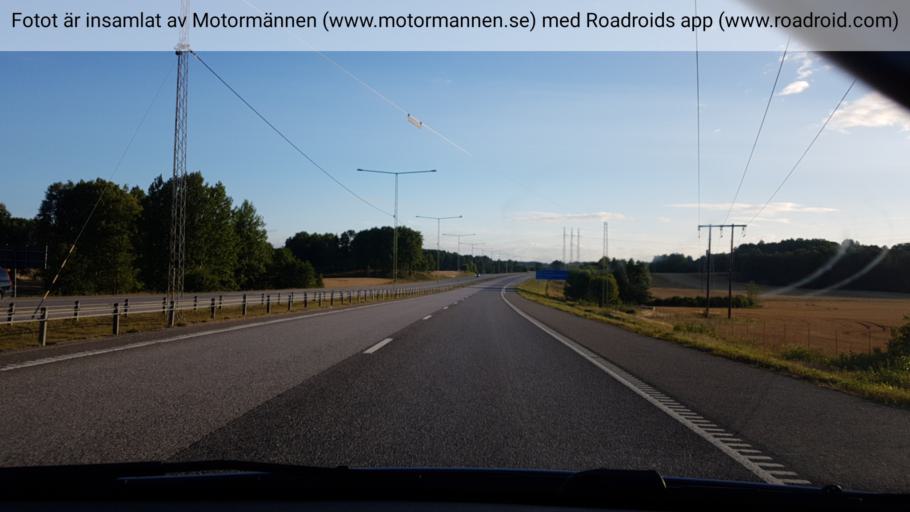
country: SE
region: Stockholm
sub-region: Haninge Kommun
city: Jordbro
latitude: 59.1154
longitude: 18.1281
